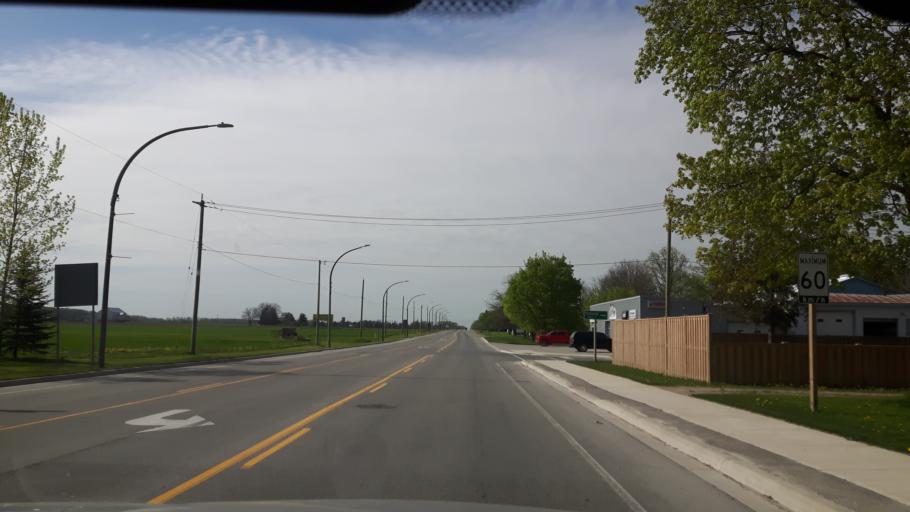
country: CA
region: Ontario
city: Bluewater
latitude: 43.4341
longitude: -81.4986
